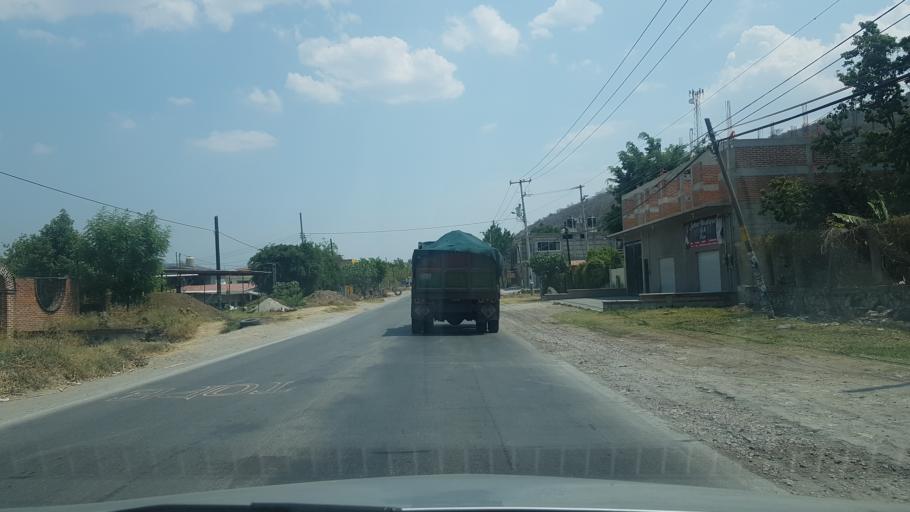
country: MX
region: Morelos
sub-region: Tlaltizapan de Zapata
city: Colonia Palo Prieto (Chipitongo)
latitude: 18.7147
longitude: -99.1187
